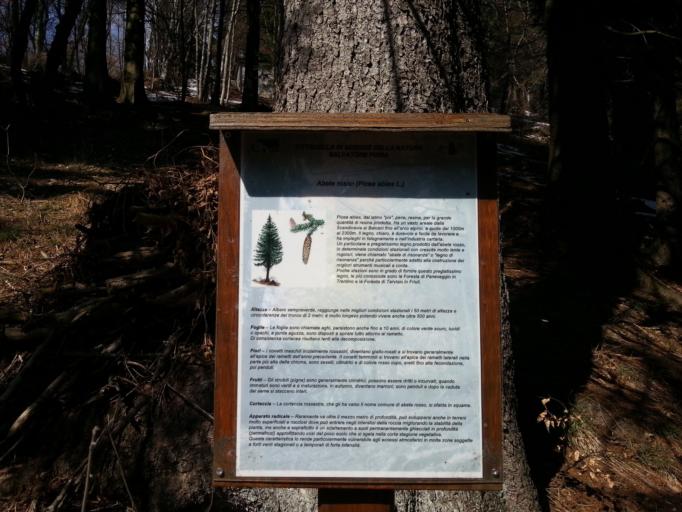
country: IT
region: Lombardy
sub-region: Provincia di Varese
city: Brinzio
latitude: 45.8674
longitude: 8.7744
